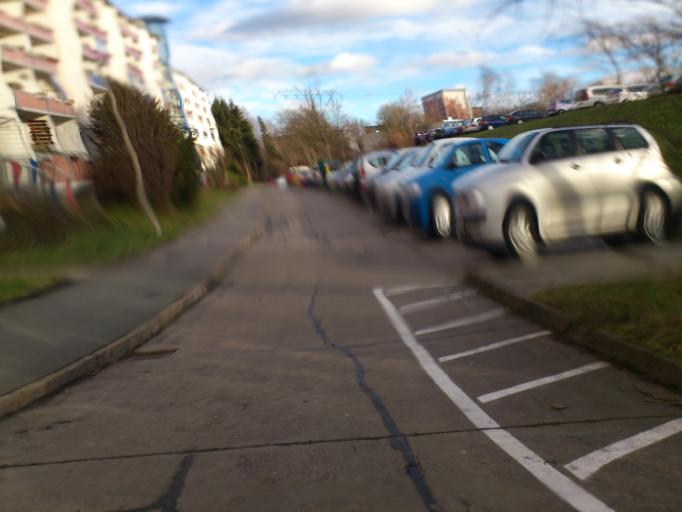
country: DE
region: Saxony
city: Neukirchen
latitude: 50.7885
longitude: 12.8957
